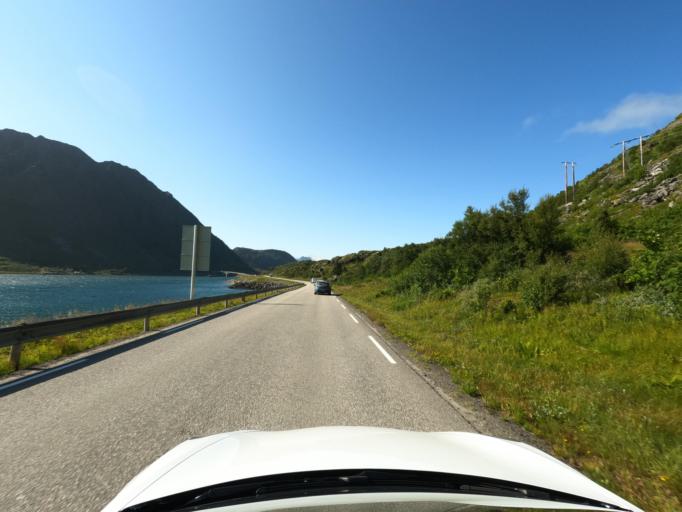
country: NO
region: Nordland
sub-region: Vagan
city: Kabelvag
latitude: 68.2650
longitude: 14.1785
